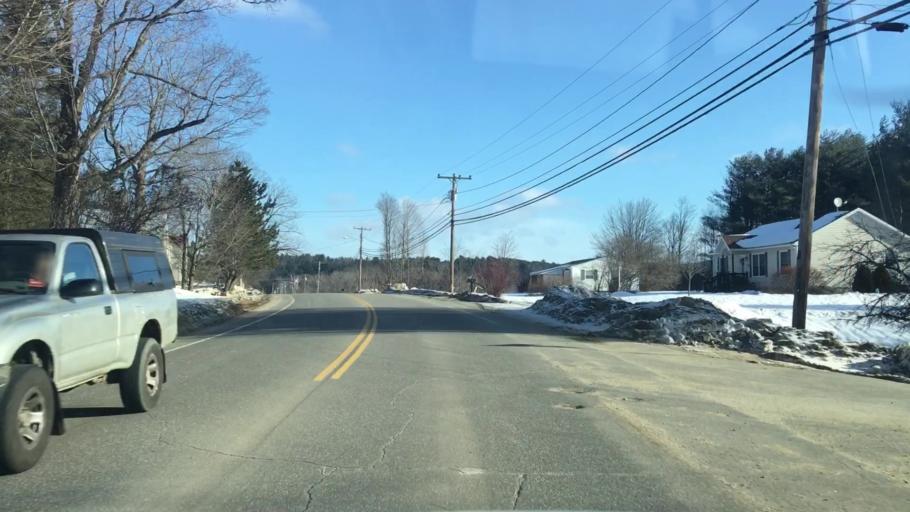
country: US
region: Maine
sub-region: Oxford County
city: West Paris
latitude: 44.3274
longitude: -70.5634
